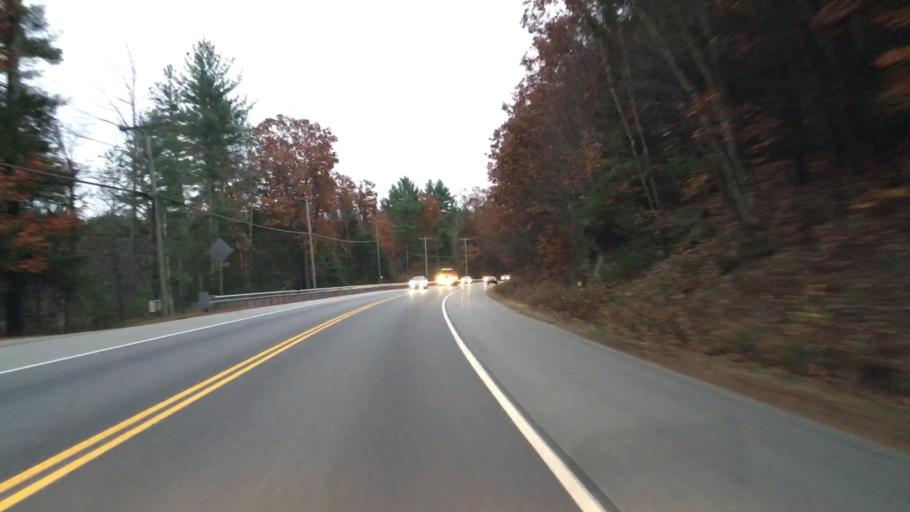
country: US
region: New Hampshire
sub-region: Hillsborough County
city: Milford
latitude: 42.8876
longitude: -71.6084
